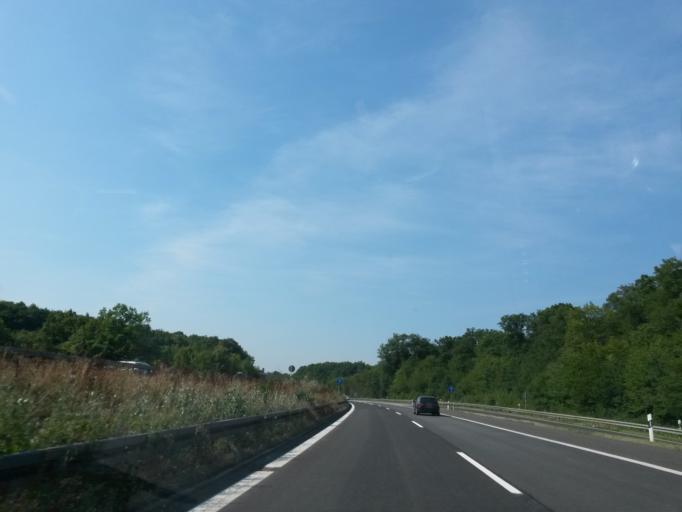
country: DE
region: Bavaria
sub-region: Regierungsbezirk Unterfranken
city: Werneck
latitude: 50.0024
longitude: 10.0785
